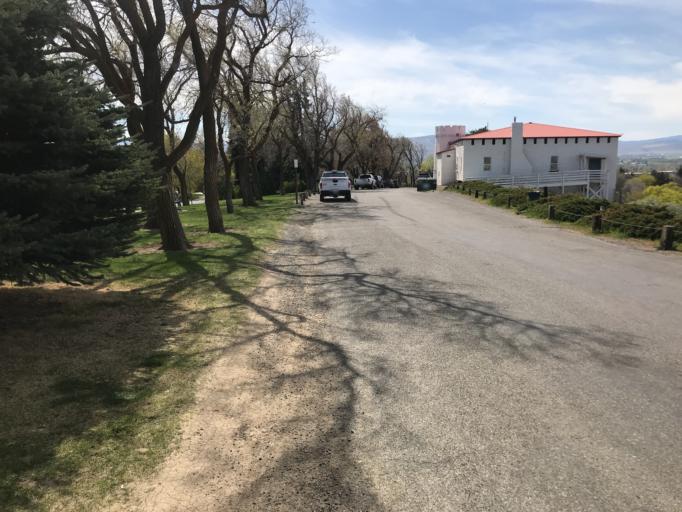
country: US
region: Washington
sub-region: Kittitas County
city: Ellensburg
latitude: 46.9982
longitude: -120.5307
